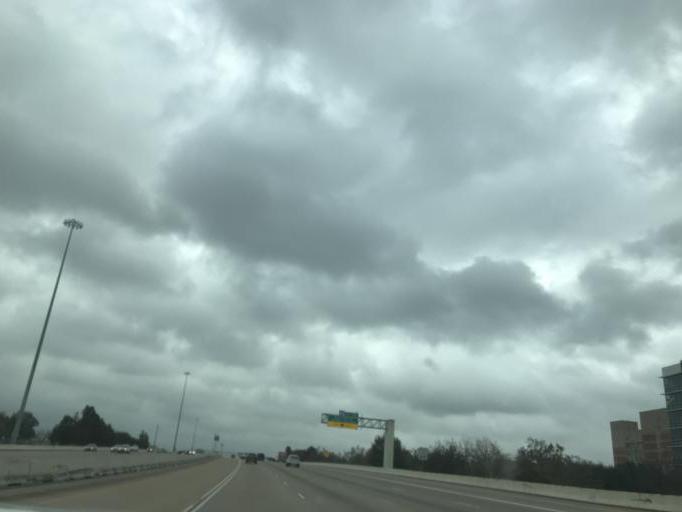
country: US
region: Texas
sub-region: Fort Bend County
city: Sugar Land
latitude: 29.5959
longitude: -95.6248
